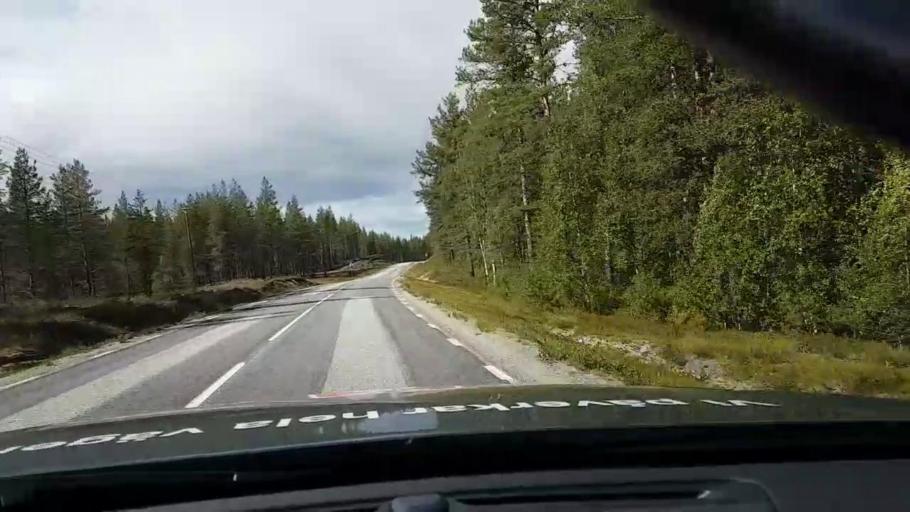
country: SE
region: Vaesterbotten
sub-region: Asele Kommun
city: Asele
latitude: 63.8542
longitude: 17.3905
